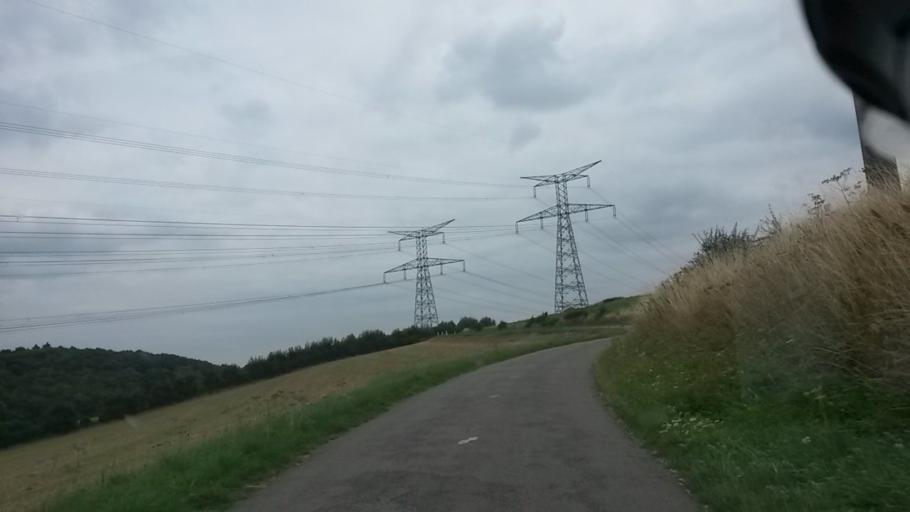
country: FR
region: Haute-Normandie
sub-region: Departement de la Seine-Maritime
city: La Feuillie
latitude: 49.4777
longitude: 1.5257
